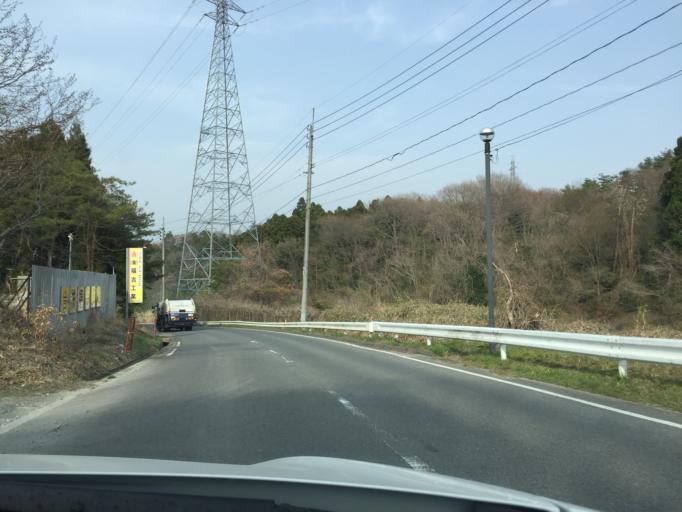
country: JP
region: Fukushima
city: Iwaki
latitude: 36.9704
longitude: 140.8540
